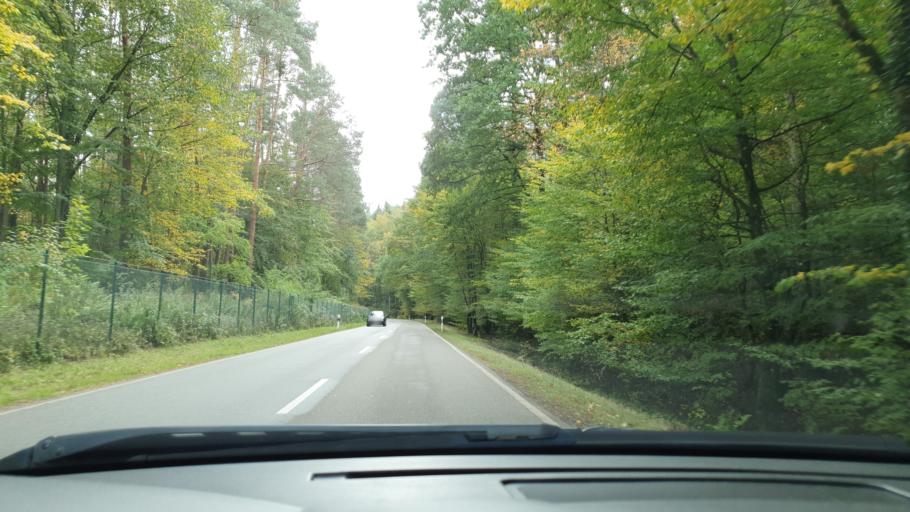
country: DE
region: Rheinland-Pfalz
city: Kaiserslautern
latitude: 49.4263
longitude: 7.8176
